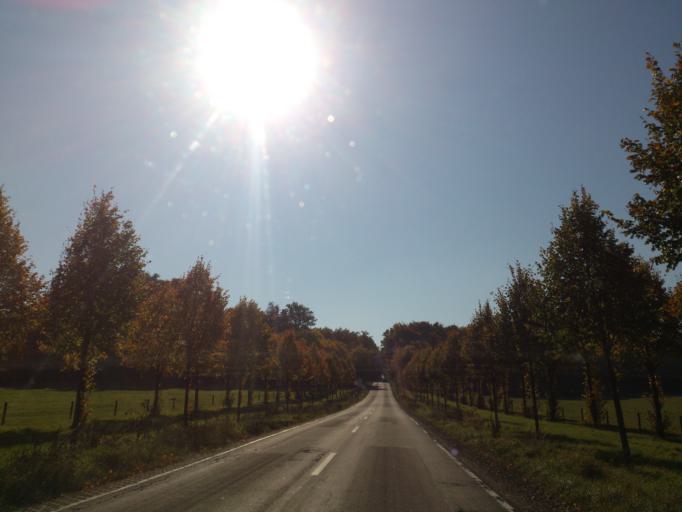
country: DE
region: Hesse
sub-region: Regierungsbezirk Kassel
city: Calden
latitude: 51.3887
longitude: 9.4168
